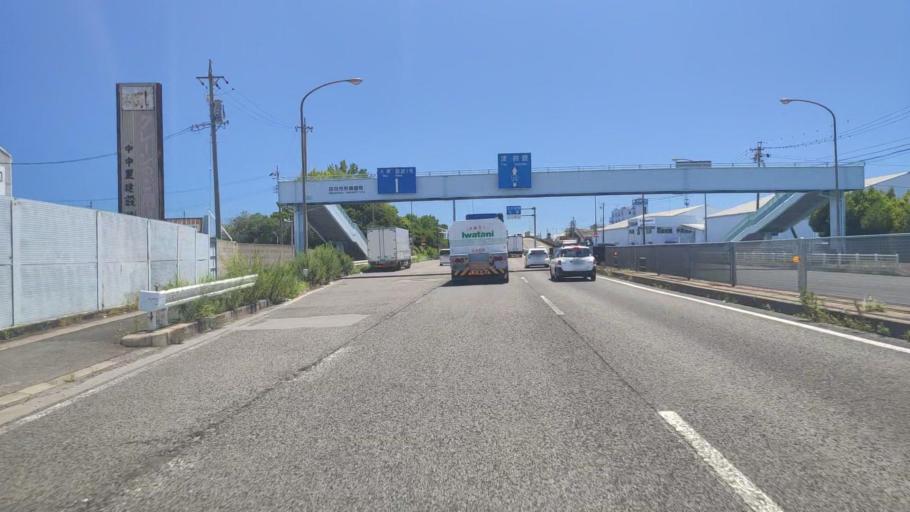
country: JP
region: Mie
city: Yokkaichi
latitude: 34.9323
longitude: 136.6153
